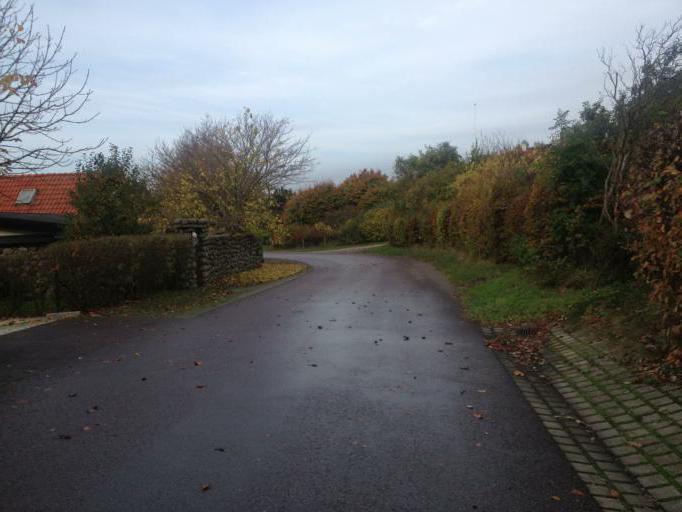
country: SE
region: Skane
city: Bjarred
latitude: 55.7135
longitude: 13.0234
